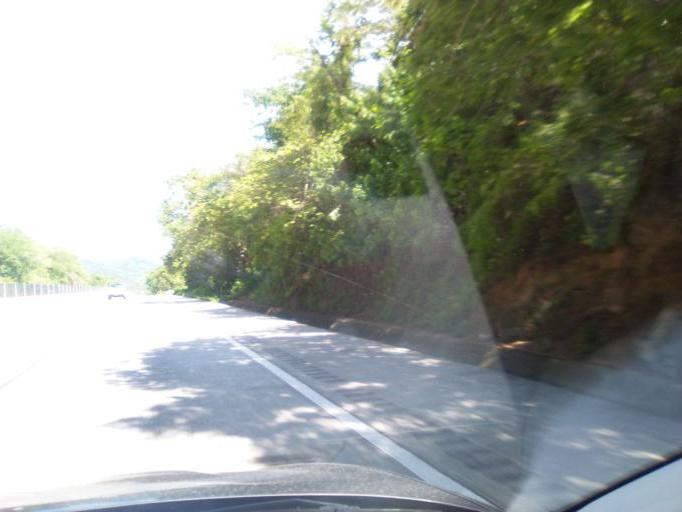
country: MX
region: Guerrero
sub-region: Acapulco de Juarez
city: Kilometro 30
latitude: 16.9822
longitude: -99.7112
